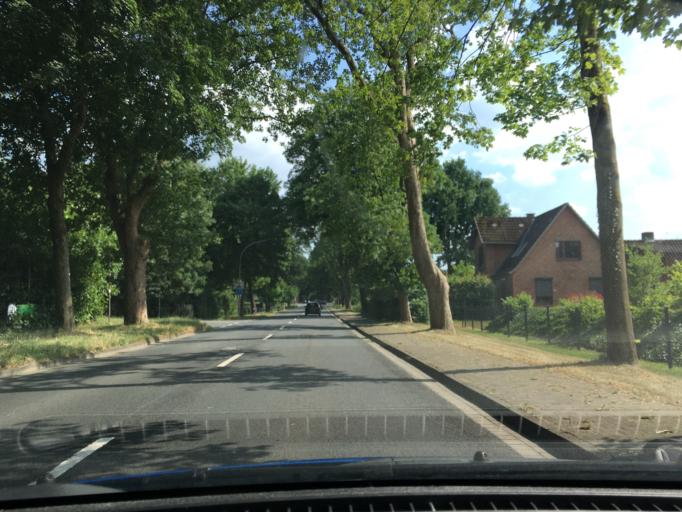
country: DE
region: Lower Saxony
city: Welle
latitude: 53.2364
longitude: 9.8029
